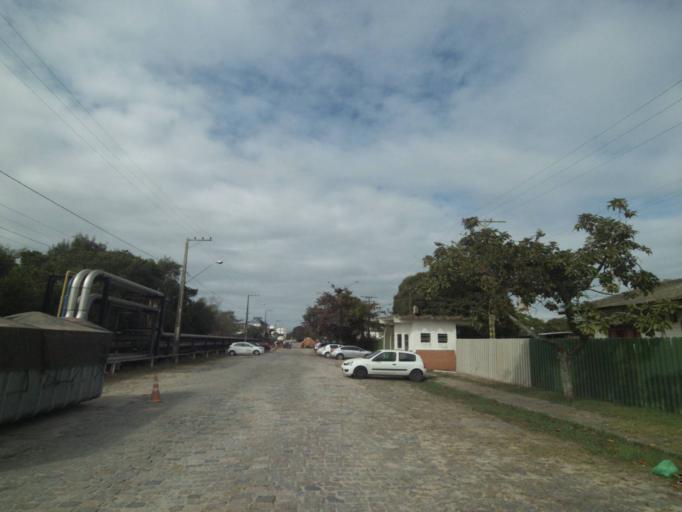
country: BR
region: Parana
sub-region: Paranagua
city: Paranagua
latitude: -25.5055
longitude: -48.5341
